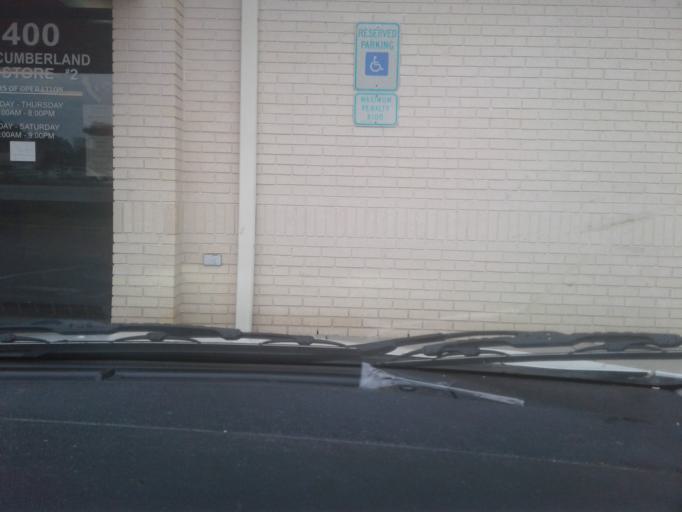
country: US
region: North Carolina
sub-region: Harnett County
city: Dunn
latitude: 35.3225
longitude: -78.6393
